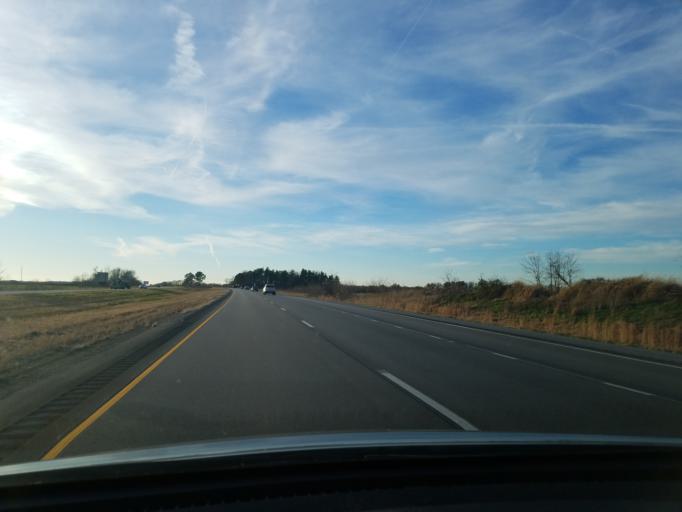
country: US
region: Indiana
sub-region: Spencer County
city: Dale
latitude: 38.1958
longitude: -86.9910
